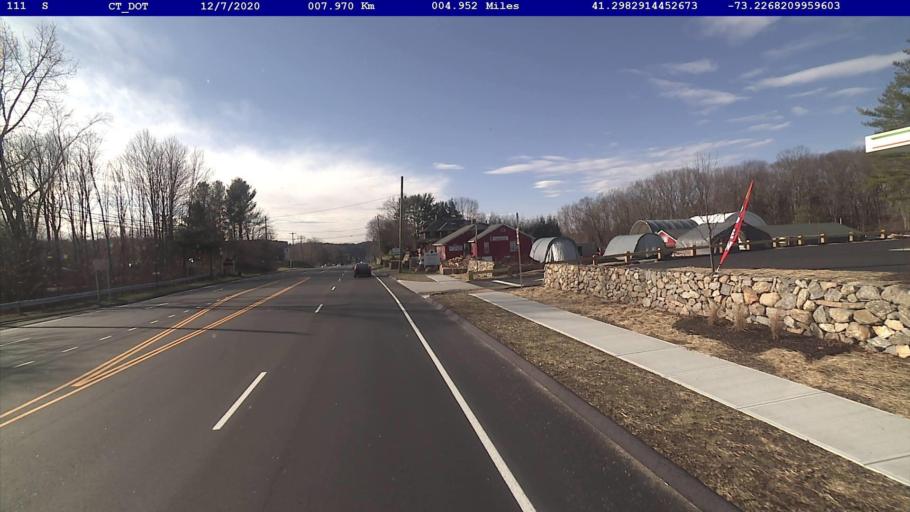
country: US
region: Connecticut
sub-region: Fairfield County
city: Trumbull
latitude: 41.2983
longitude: -73.2268
